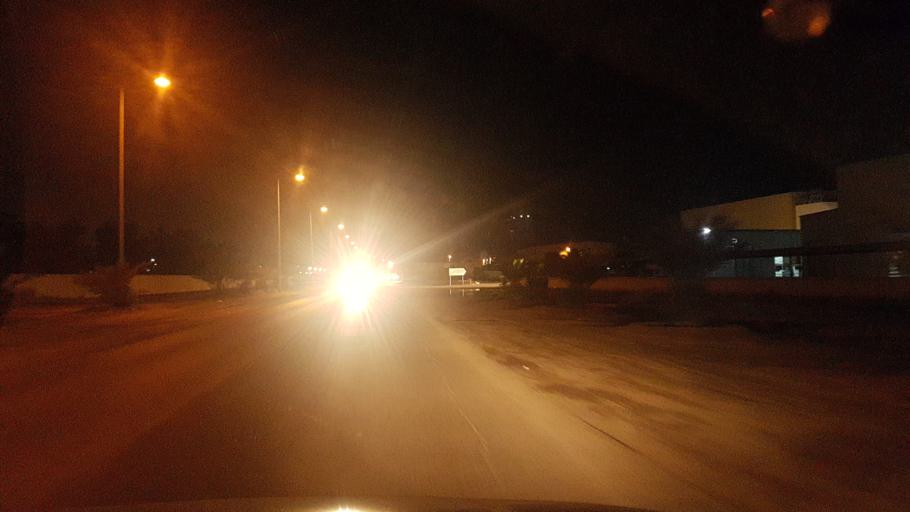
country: BH
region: Muharraq
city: Al Hadd
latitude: 26.2746
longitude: 50.6426
